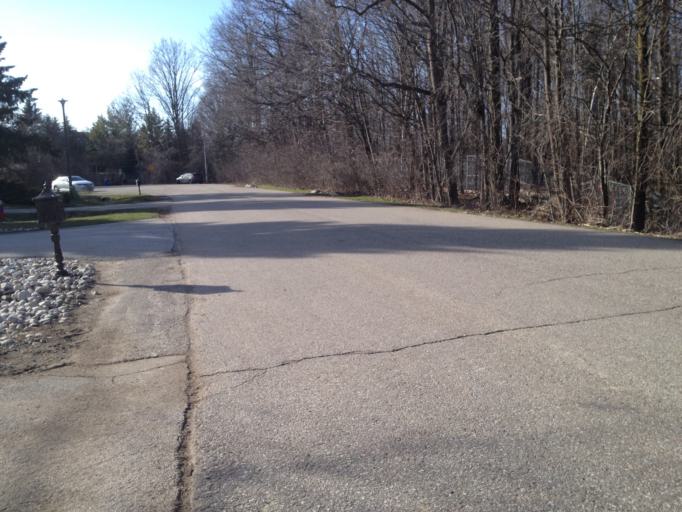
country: CA
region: Ontario
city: Brampton
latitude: 43.7437
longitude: -79.8030
